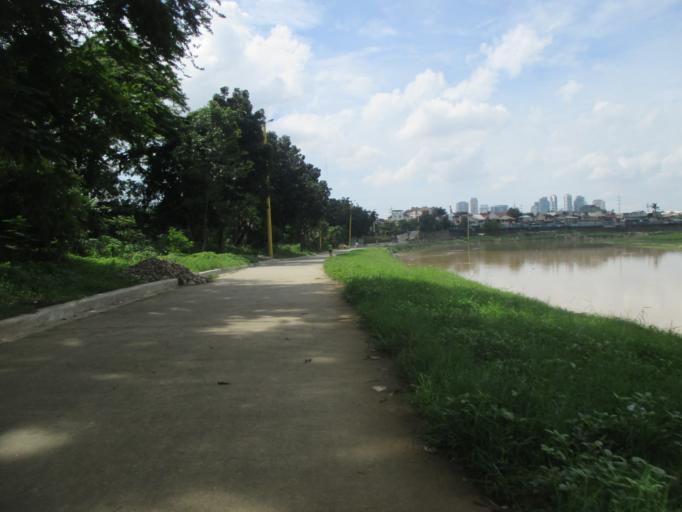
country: PH
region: Metro Manila
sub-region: Marikina
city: Calumpang
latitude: 14.6263
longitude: 121.0942
